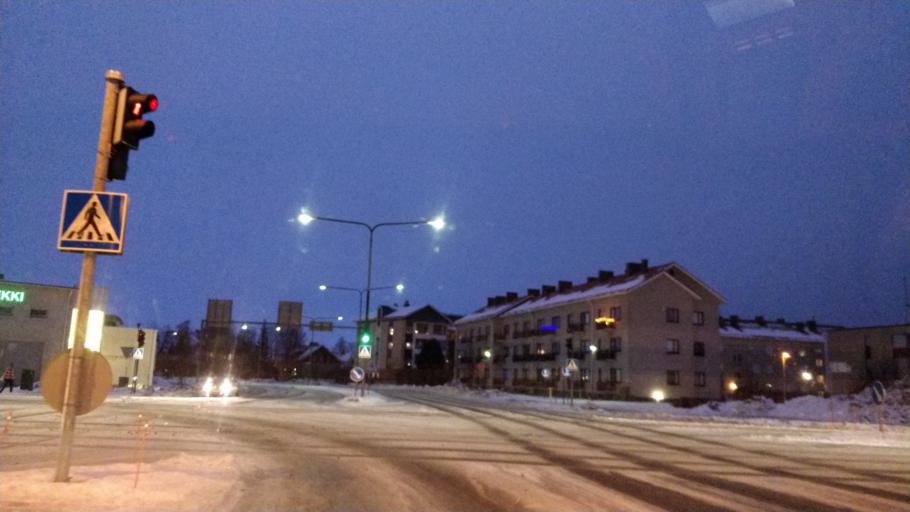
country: FI
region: Lapland
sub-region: Kemi-Tornio
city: Kemi
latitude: 65.7405
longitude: 24.5656
